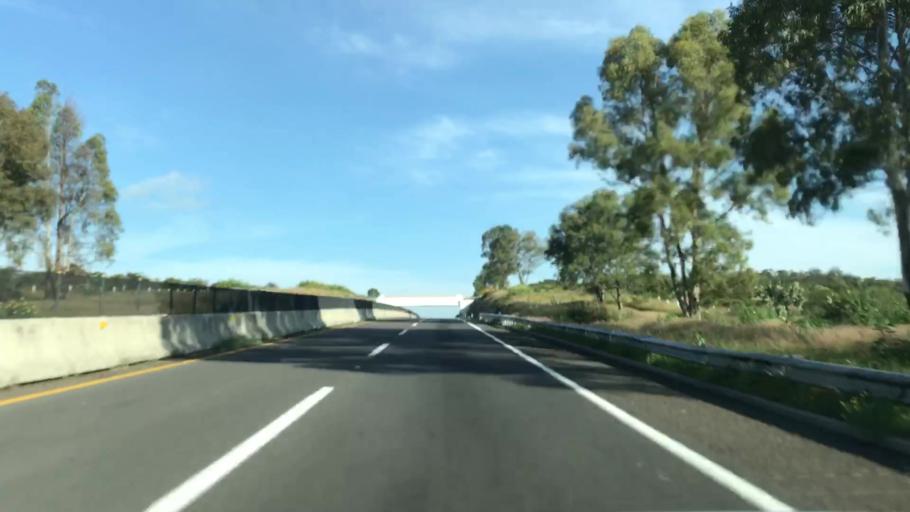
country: MX
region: Jalisco
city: Encarnacion de Diaz
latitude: 21.3821
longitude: -102.1396
